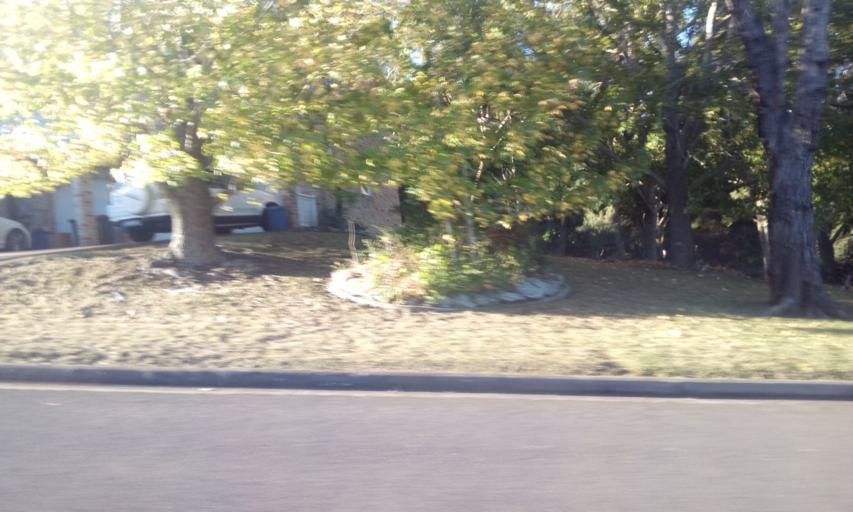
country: AU
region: New South Wales
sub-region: Wollongong
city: Mount Keira
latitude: -34.4233
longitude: 150.8483
